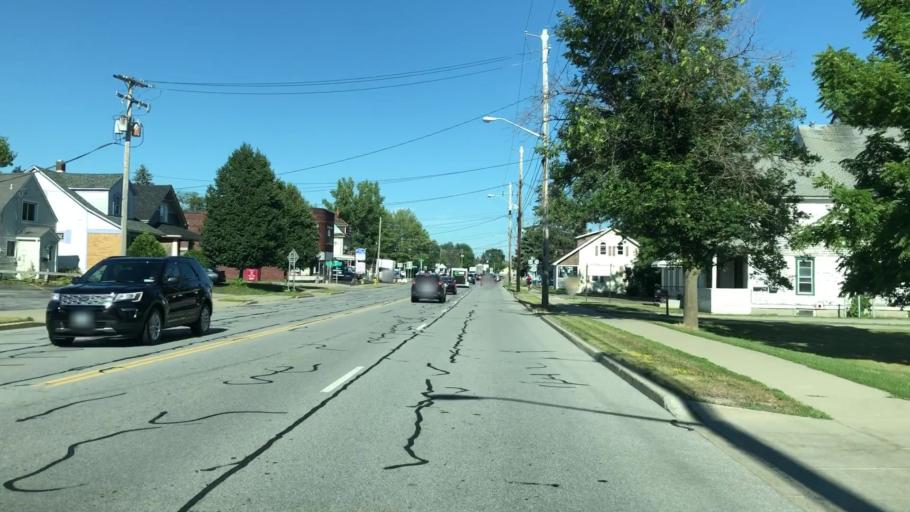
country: US
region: New York
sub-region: Erie County
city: Depew
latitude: 42.9018
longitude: -78.7000
